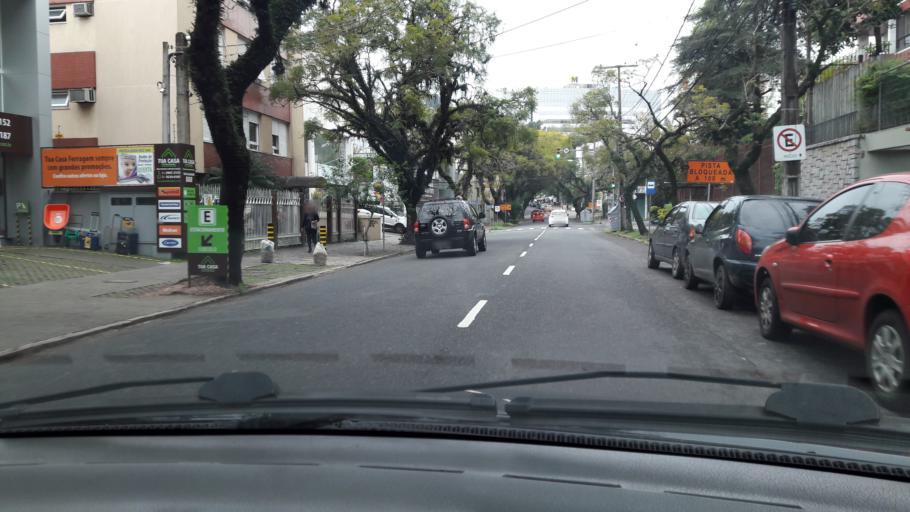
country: BR
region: Rio Grande do Sul
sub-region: Porto Alegre
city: Porto Alegre
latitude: -30.0266
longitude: -51.1870
